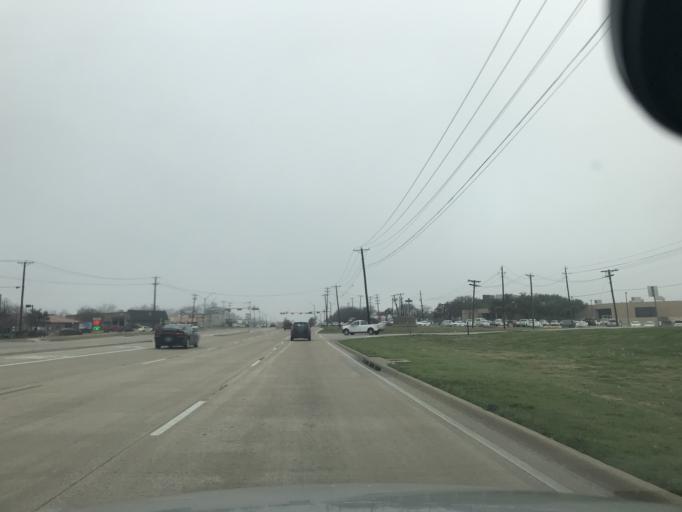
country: US
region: Texas
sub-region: Collin County
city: Wylie
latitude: 33.0184
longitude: -96.5298
